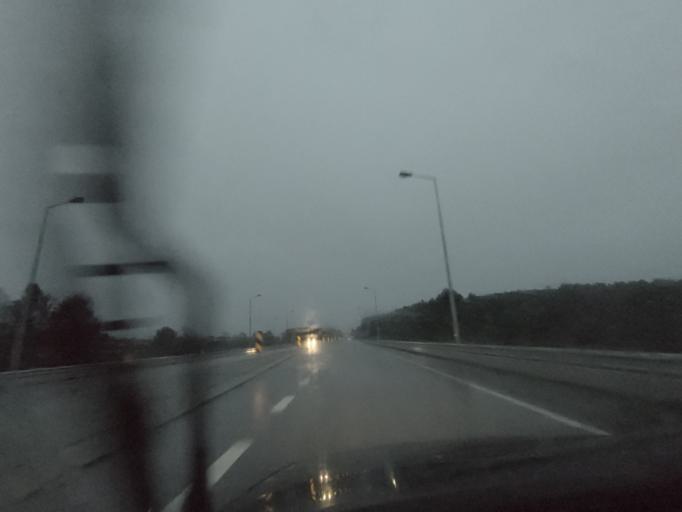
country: PT
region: Vila Real
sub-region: Sabrosa
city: Vilela
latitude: 41.2661
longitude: -7.6362
